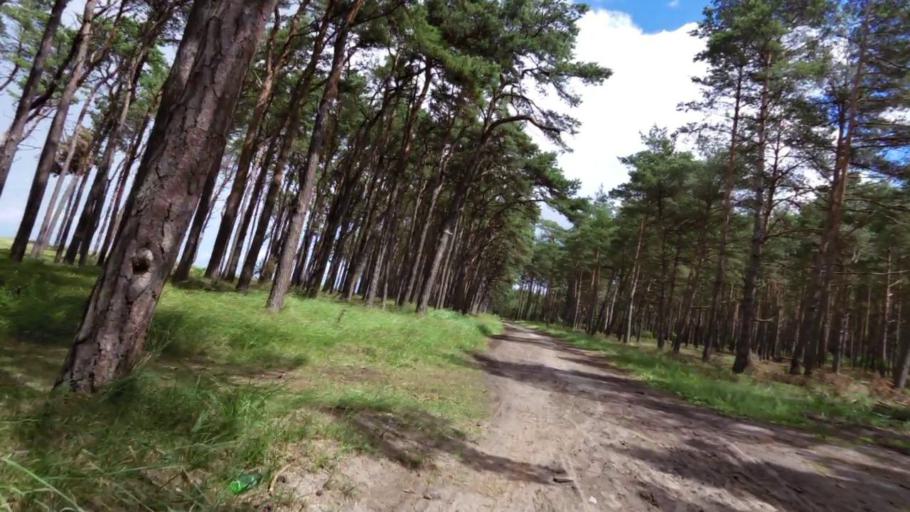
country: PL
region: West Pomeranian Voivodeship
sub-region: Powiat slawienski
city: Darlowo
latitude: 54.4971
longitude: 16.4495
